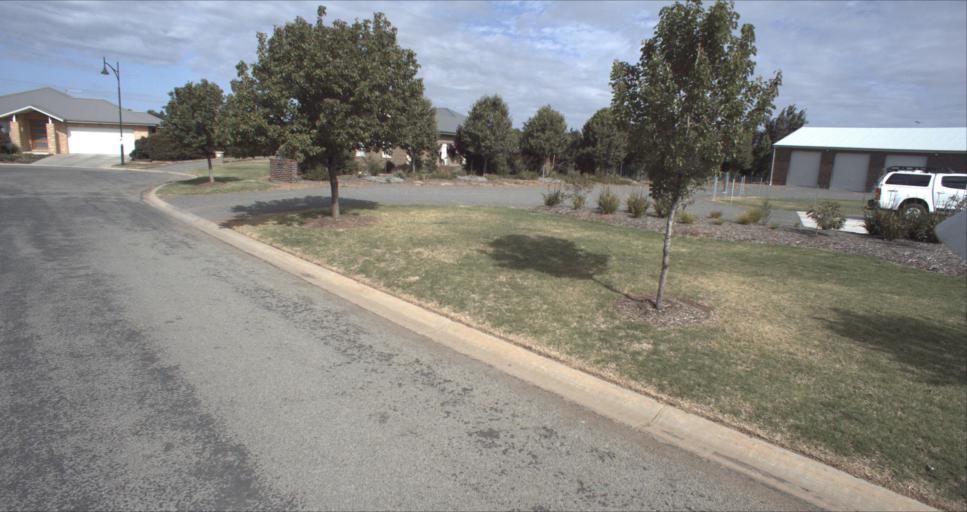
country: AU
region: New South Wales
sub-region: Leeton
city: Leeton
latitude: -34.5605
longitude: 146.4280
